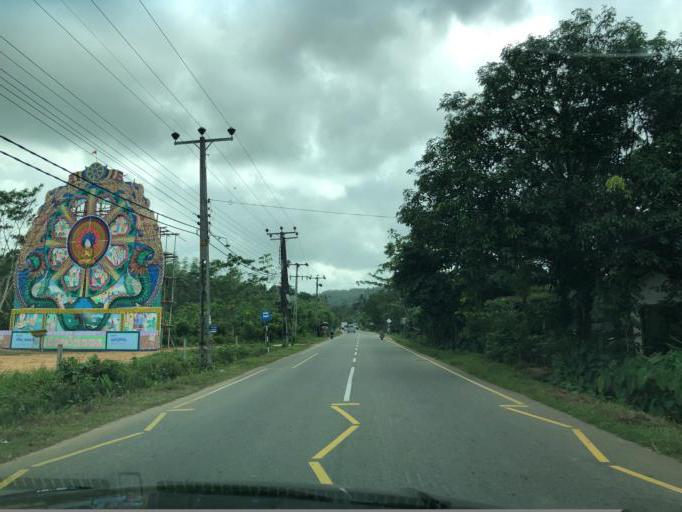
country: LK
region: Western
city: Horana South
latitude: 6.6786
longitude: 80.1591
